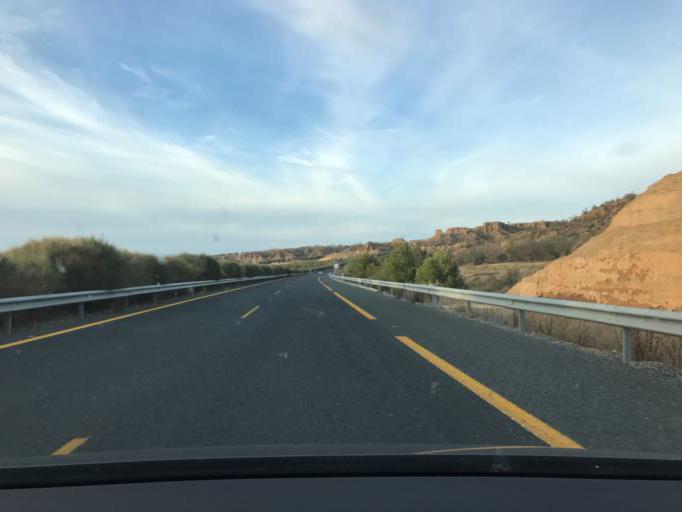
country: ES
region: Andalusia
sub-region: Provincia de Granada
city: Guadix
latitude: 37.3031
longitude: -3.1108
